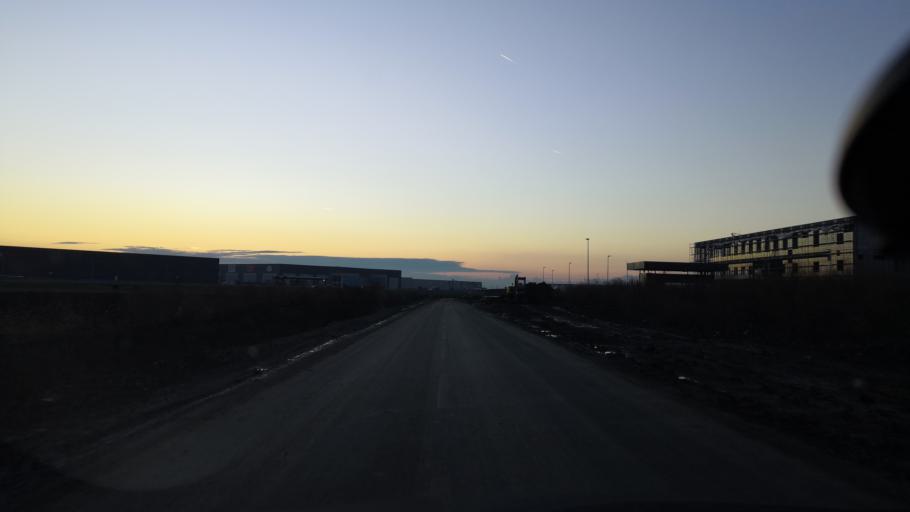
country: RS
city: Simanovci
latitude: 44.8894
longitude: 20.0994
